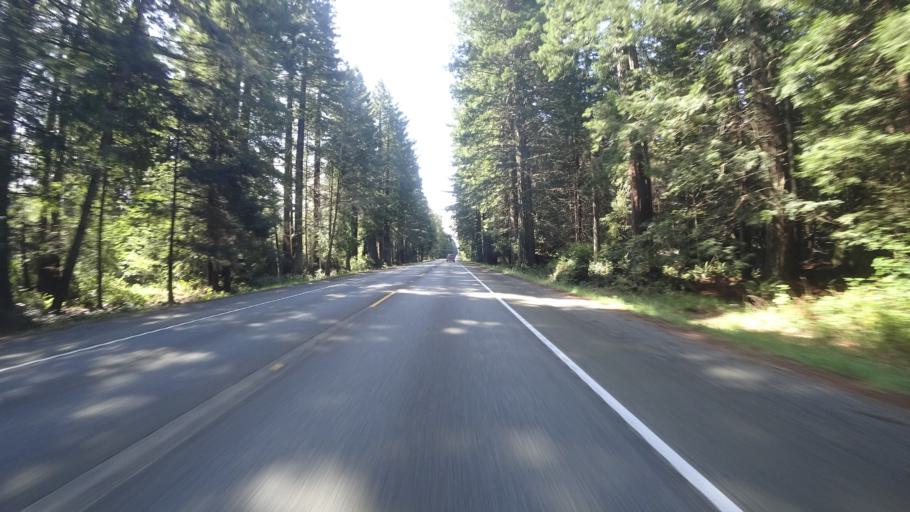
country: US
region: California
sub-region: Del Norte County
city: Bertsch-Oceanview
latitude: 41.8281
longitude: -124.1448
